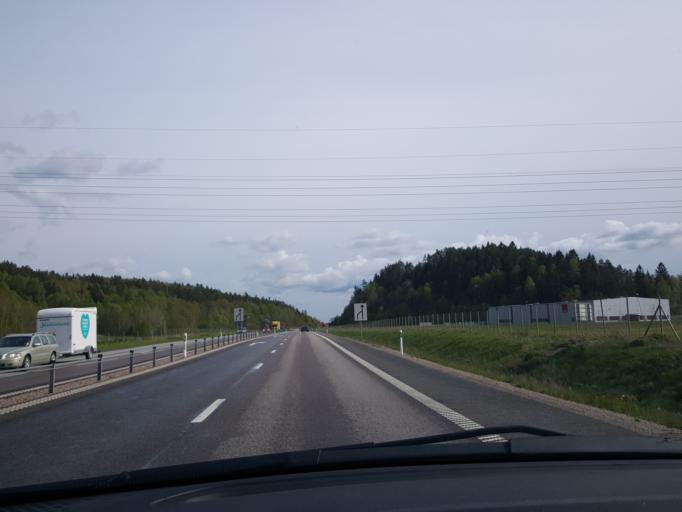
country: SE
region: Vaestra Goetaland
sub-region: Lilla Edets Kommun
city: Lilla Edet
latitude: 58.1192
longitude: 12.1398
